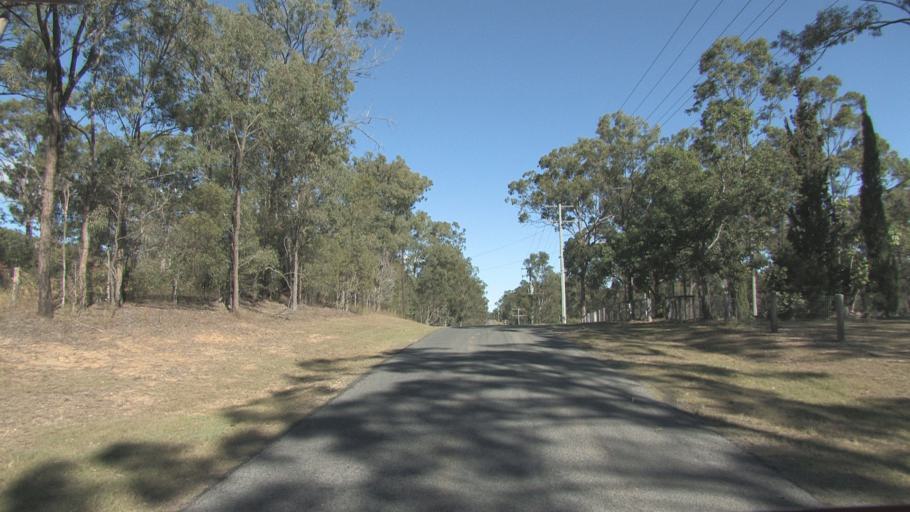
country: AU
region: Queensland
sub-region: Logan
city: Chambers Flat
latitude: -27.8094
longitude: 153.0786
